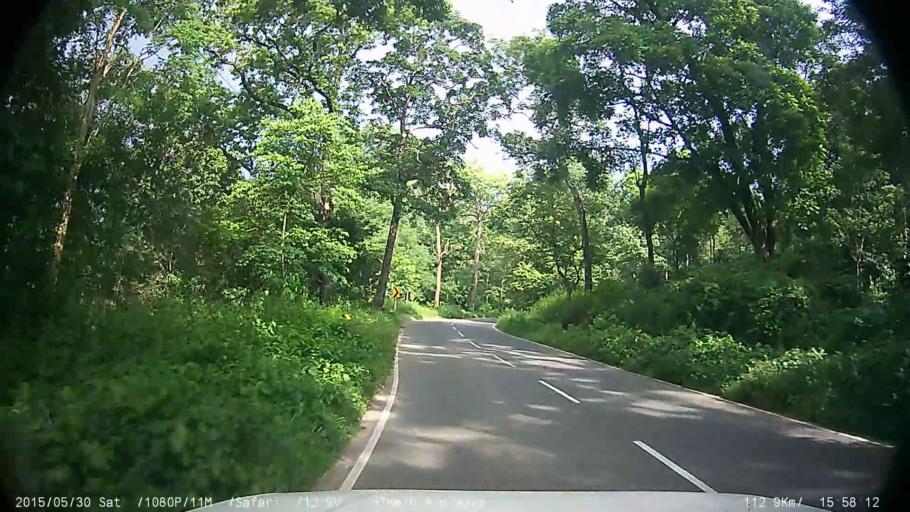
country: IN
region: Kerala
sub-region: Wayanad
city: Kalpetta
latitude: 11.6505
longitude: 76.0878
